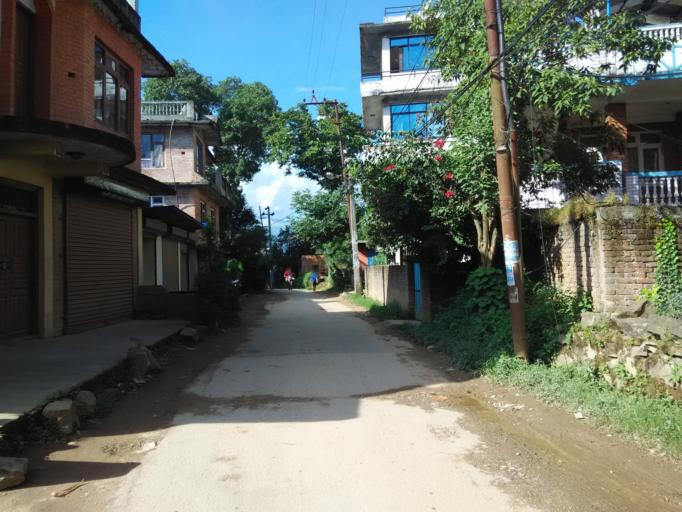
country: NP
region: Central Region
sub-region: Bagmati Zone
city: Patan
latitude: 27.6082
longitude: 85.3545
